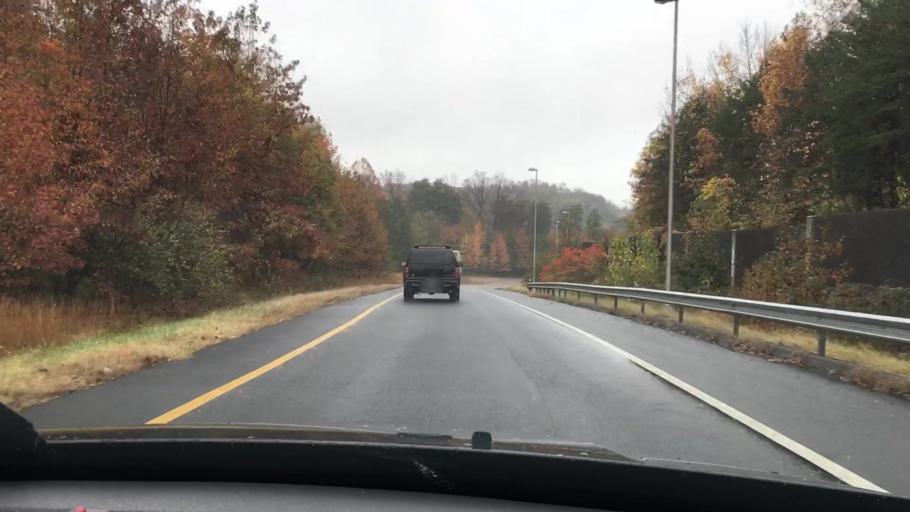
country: US
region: Virginia
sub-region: Fairfax County
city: Greenbriar
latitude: 38.8520
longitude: -77.3891
